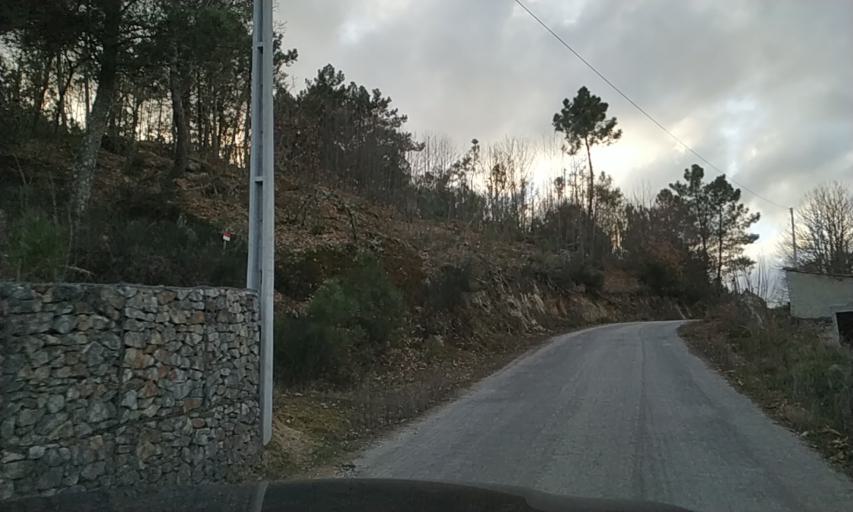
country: PT
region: Braganca
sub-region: Carrazeda de Ansiaes
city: Carrazeda de Anciaes
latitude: 41.2211
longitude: -7.3508
